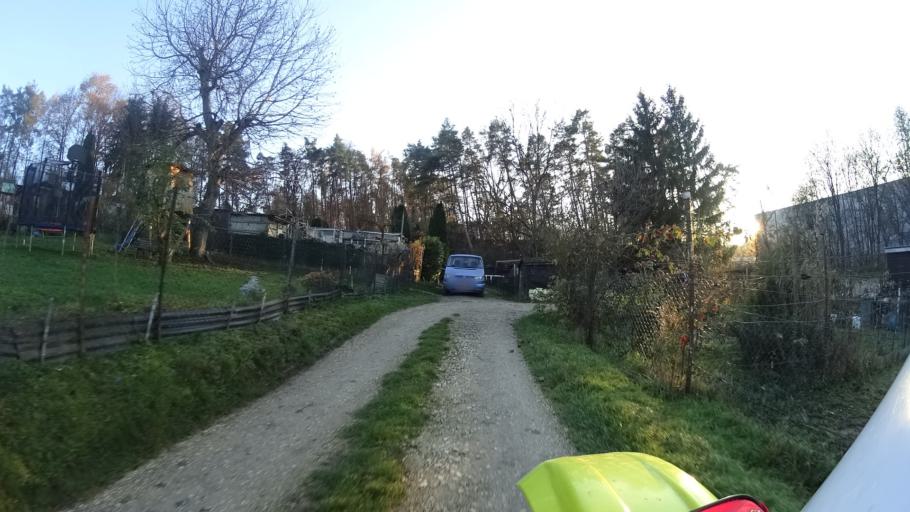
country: DE
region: Baden-Wuerttemberg
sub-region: Regierungsbezirk Stuttgart
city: Eislingen
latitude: 48.6766
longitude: 9.6900
